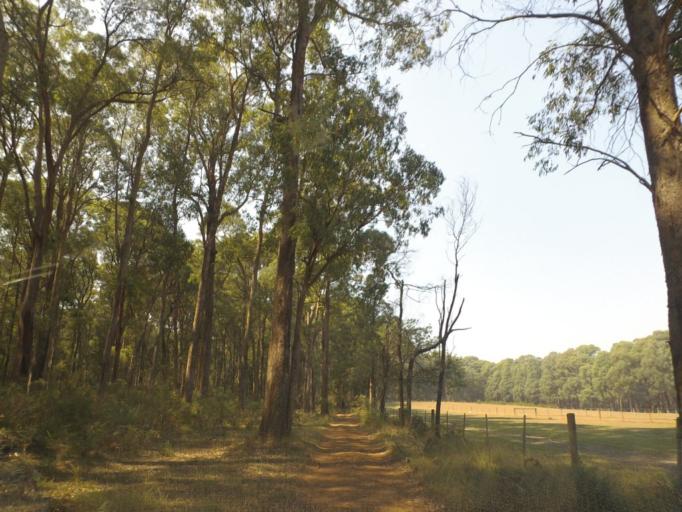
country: AU
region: Victoria
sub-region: Yarra Ranges
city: Healesville
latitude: -37.5712
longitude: 145.6531
